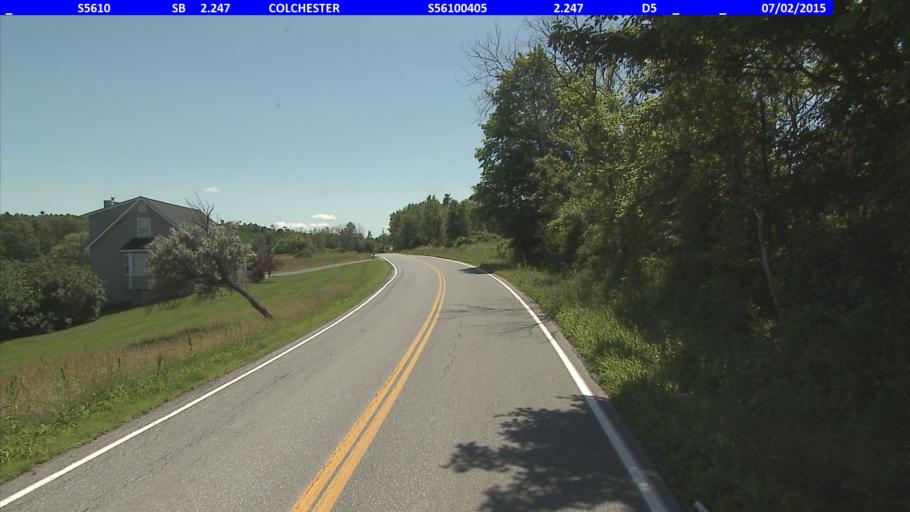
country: US
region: Vermont
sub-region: Chittenden County
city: Colchester
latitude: 44.5720
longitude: -73.1275
